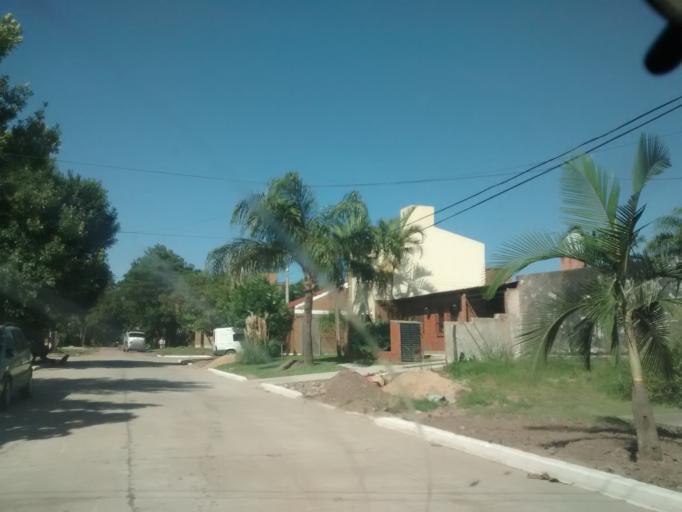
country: AR
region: Chaco
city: Resistencia
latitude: -27.4380
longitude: -58.9701
